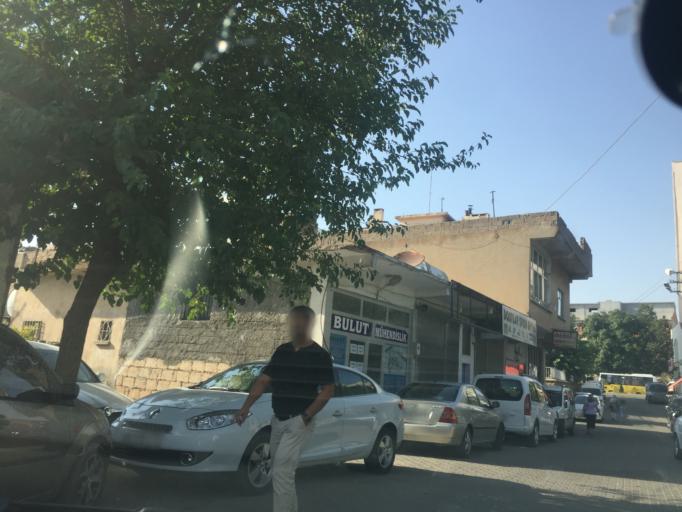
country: TR
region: Mardin
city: Midyat
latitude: 37.4147
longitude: 41.3723
